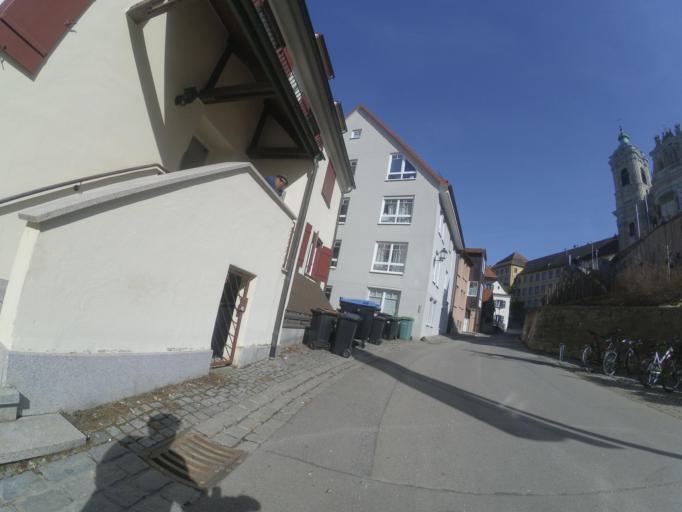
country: DE
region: Baden-Wuerttemberg
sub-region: Tuebingen Region
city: Weingarten
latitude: 47.8089
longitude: 9.6427
